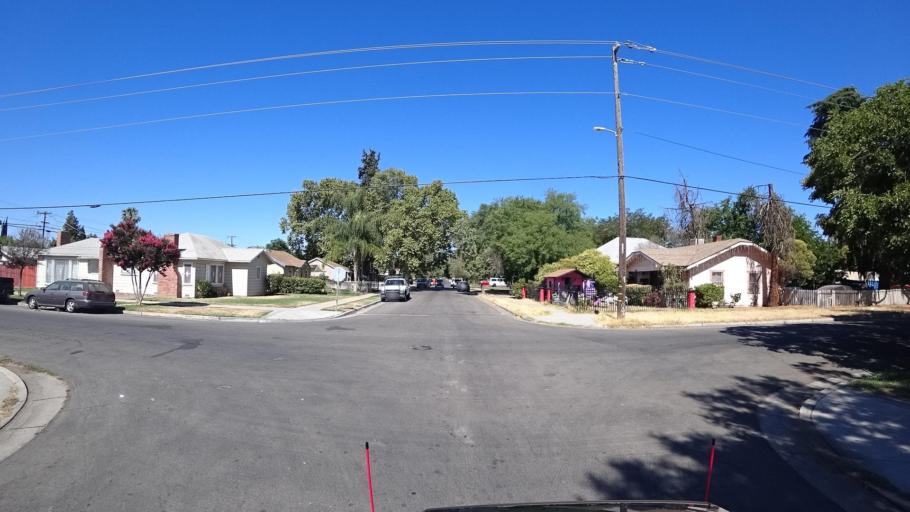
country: US
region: California
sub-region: Fresno County
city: Fresno
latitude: 36.7804
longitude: -119.7950
